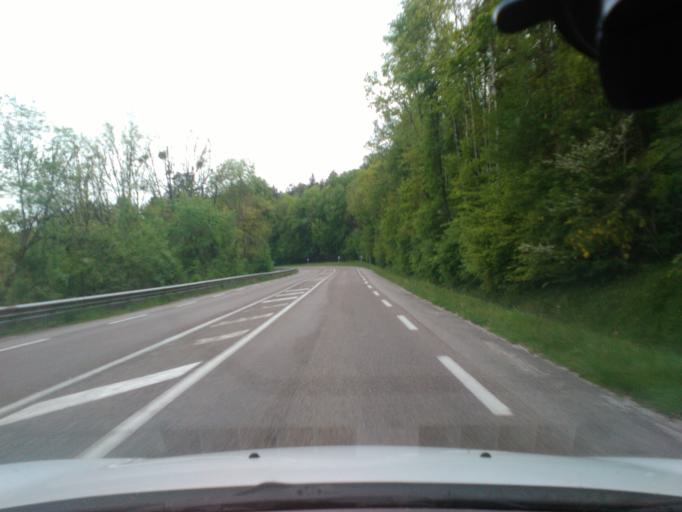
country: FR
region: Champagne-Ardenne
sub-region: Departement de la Haute-Marne
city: Chaumont
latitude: 48.1386
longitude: 5.0502
